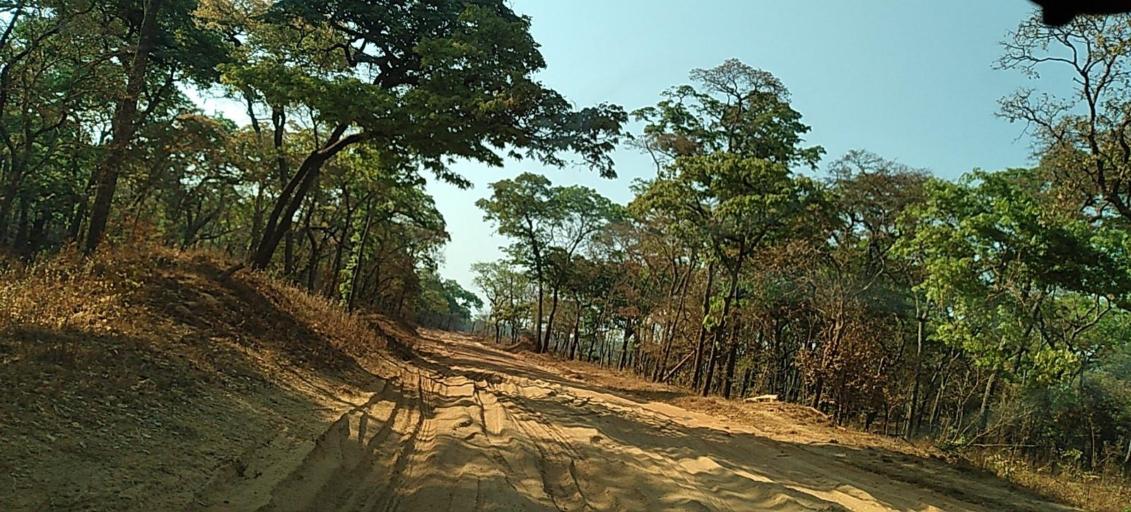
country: ZM
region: North-Western
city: Kasempa
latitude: -13.6335
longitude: 25.9906
